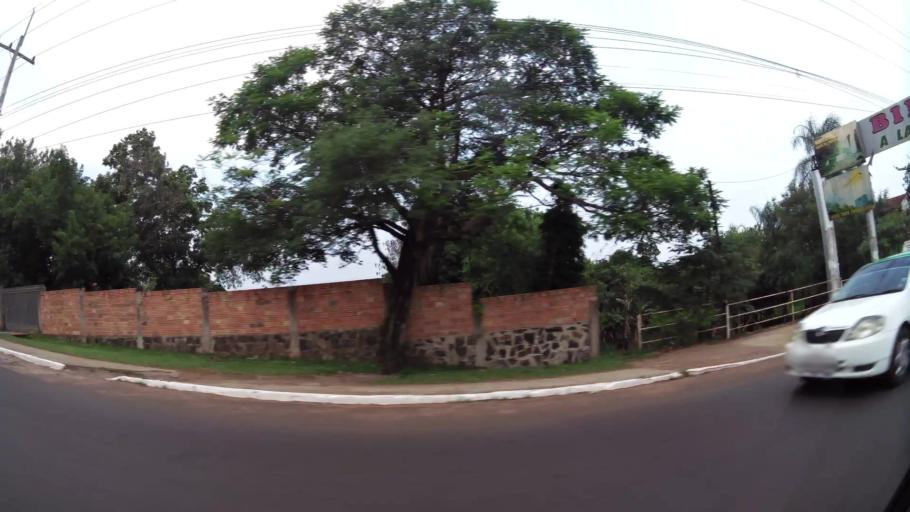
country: PY
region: Alto Parana
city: Presidente Franco
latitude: -25.5473
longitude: -54.6086
